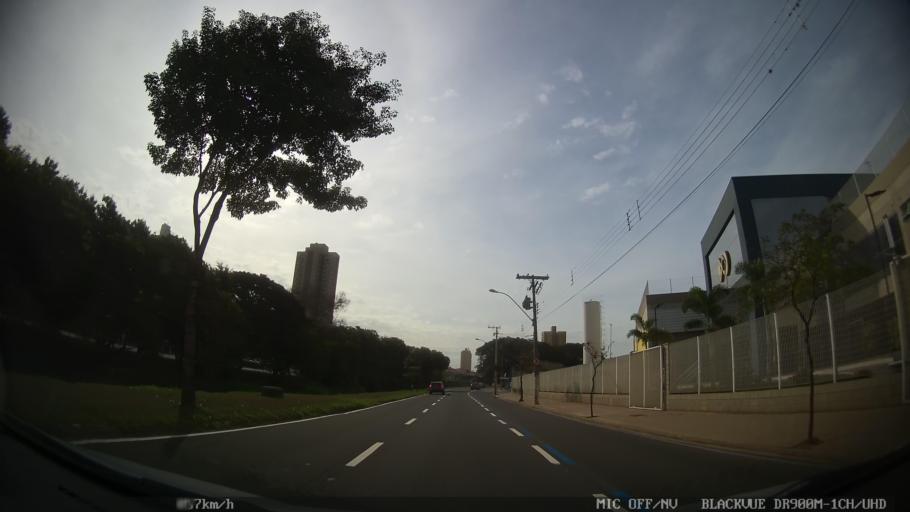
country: BR
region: Sao Paulo
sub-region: Piracicaba
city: Piracicaba
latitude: -22.7270
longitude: -47.6270
